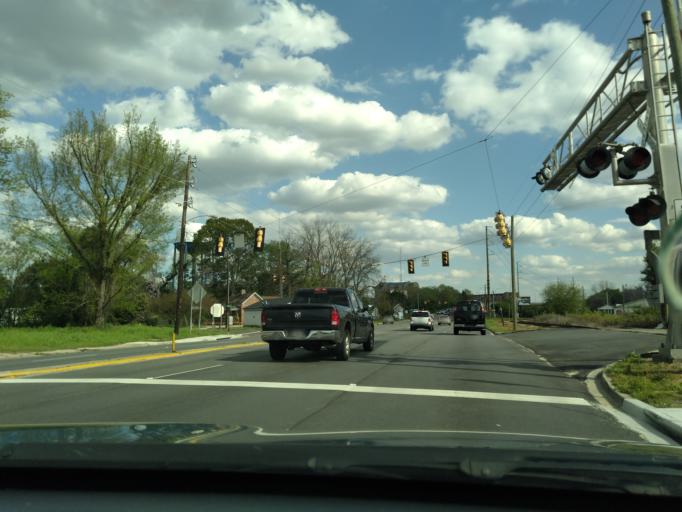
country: US
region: South Carolina
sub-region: Florence County
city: Florence
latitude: 34.2023
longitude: -79.7655
